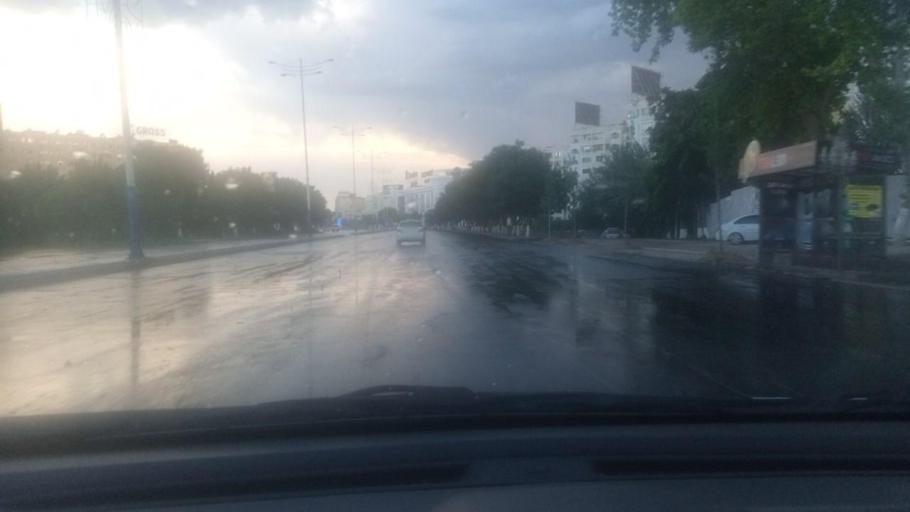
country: UZ
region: Toshkent Shahri
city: Tashkent
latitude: 41.3122
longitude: 69.2391
